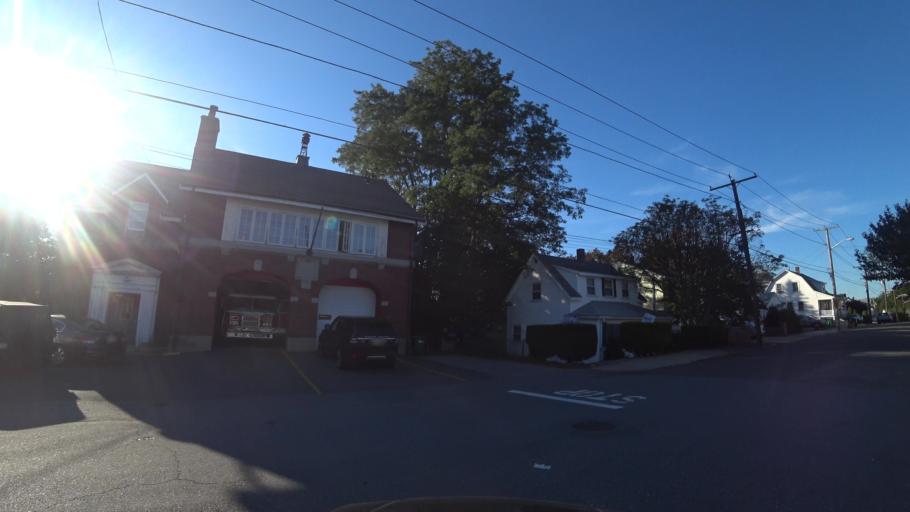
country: US
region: Massachusetts
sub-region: Middlesex County
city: Medford
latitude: 42.4358
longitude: -71.0964
